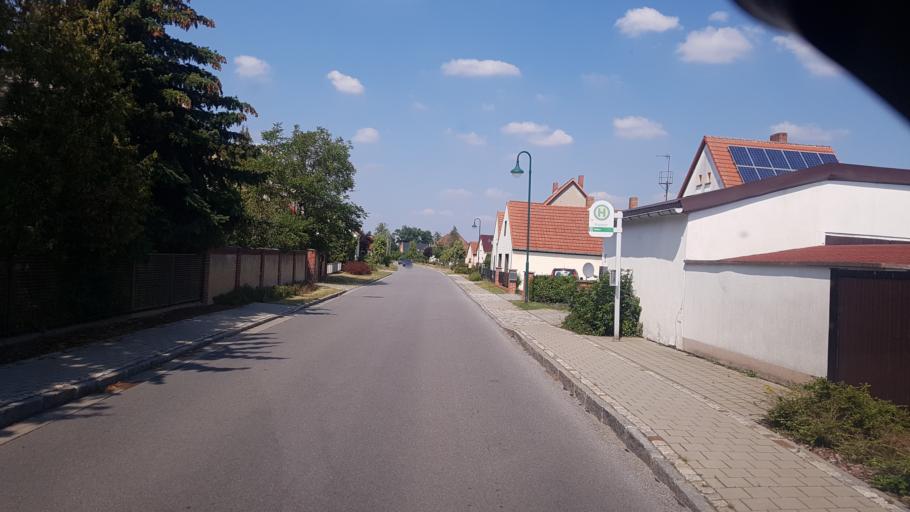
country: DE
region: Brandenburg
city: Cottbus
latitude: 51.6975
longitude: 14.4268
